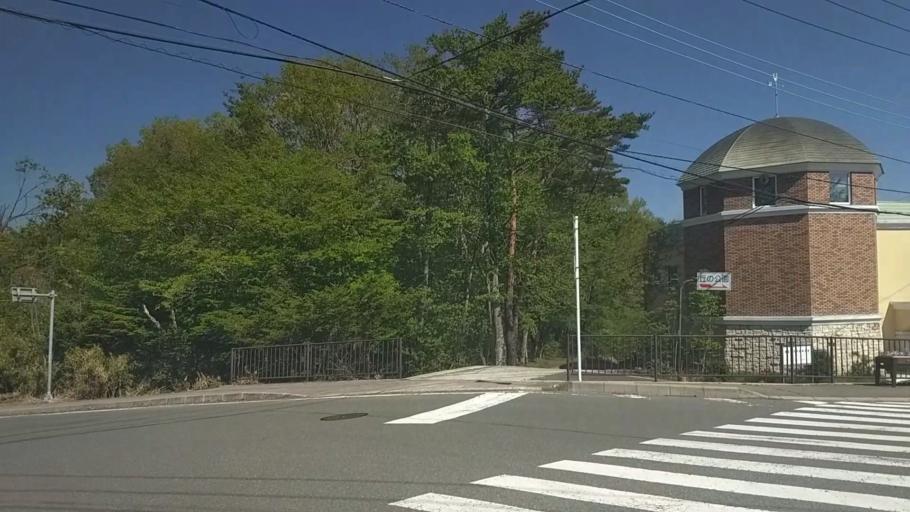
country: JP
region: Yamanashi
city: Nirasaki
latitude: 35.9175
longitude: 138.4342
